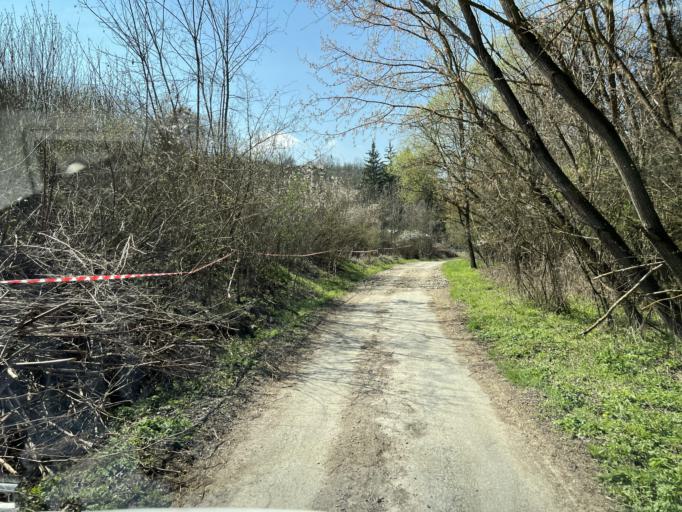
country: HU
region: Pest
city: Szob
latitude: 47.8241
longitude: 18.9018
